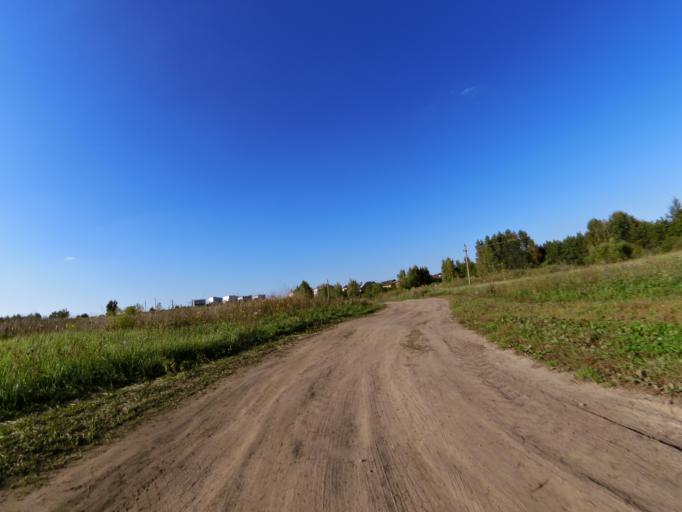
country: LT
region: Vilnius County
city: Pilaite
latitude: 54.7207
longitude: 25.1814
